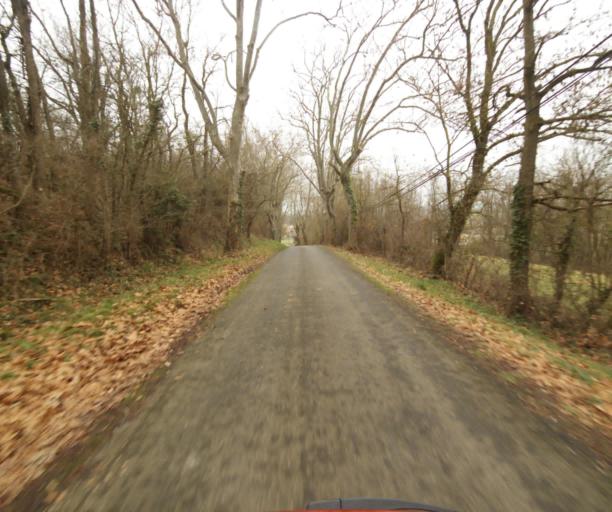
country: FR
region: Midi-Pyrenees
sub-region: Departement de la Haute-Garonne
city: Gaillac-Toulza
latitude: 43.2647
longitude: 1.5133
